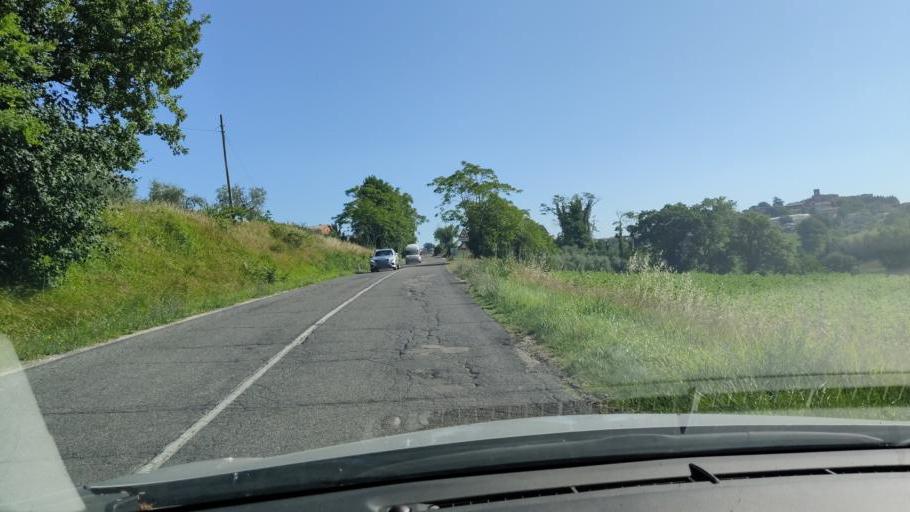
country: IT
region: Umbria
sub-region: Provincia di Terni
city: Avigliano Umbro
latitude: 42.6470
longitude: 12.4186
